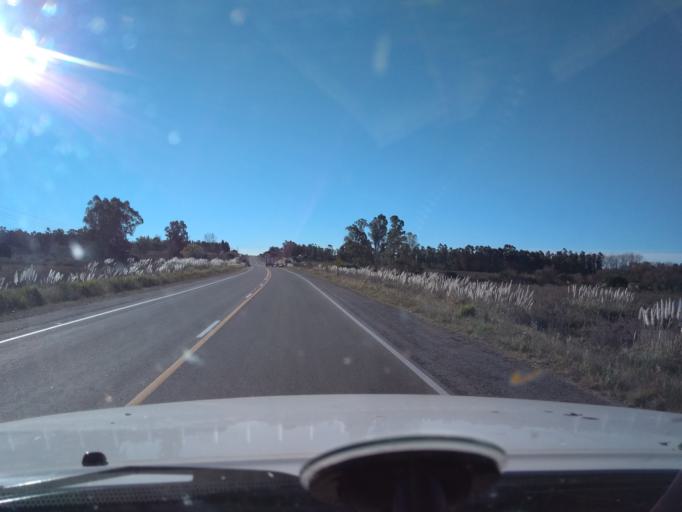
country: UY
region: Canelones
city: Sauce
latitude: -34.5961
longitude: -56.0512
